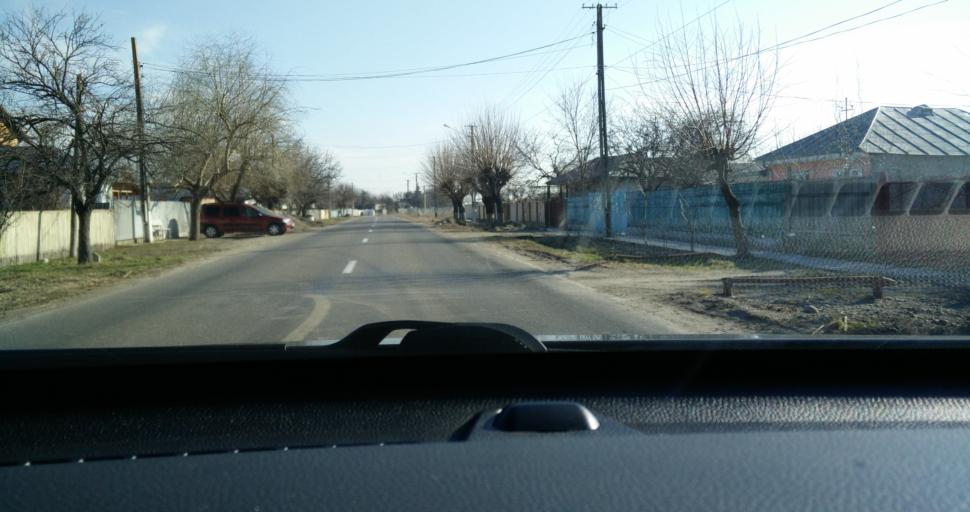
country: RO
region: Vrancea
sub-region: Comuna Nanesti
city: Nanesti
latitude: 45.5371
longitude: 27.4978
